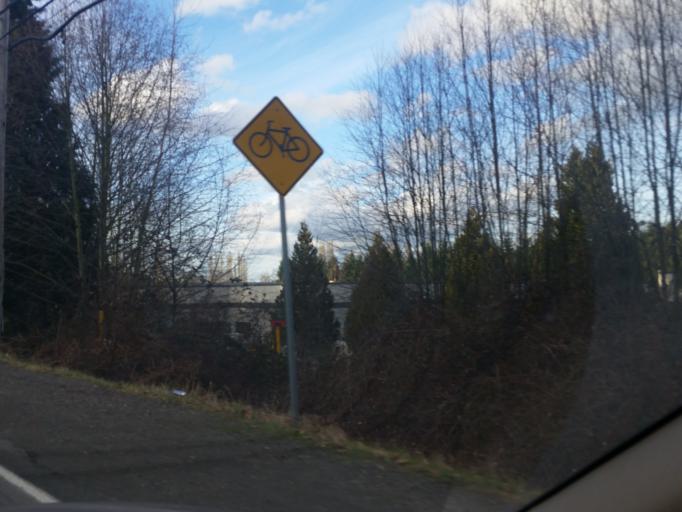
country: US
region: Washington
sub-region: King County
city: Woodinville
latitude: 47.7540
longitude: -122.1720
